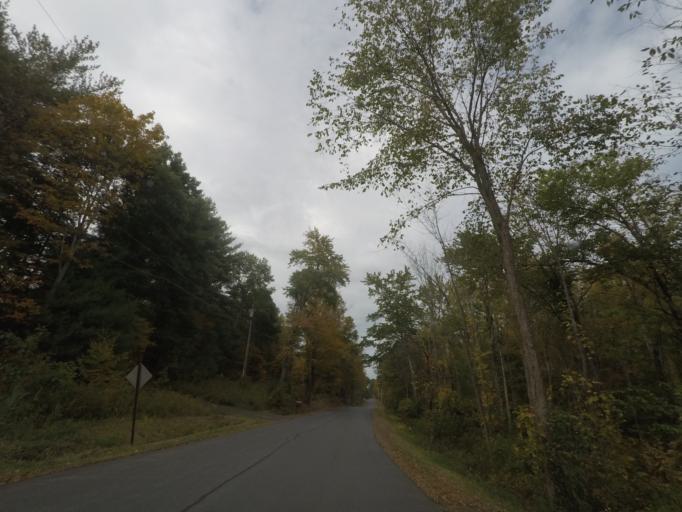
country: US
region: New York
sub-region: Rensselaer County
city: Nassau
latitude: 42.5358
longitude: -73.6453
